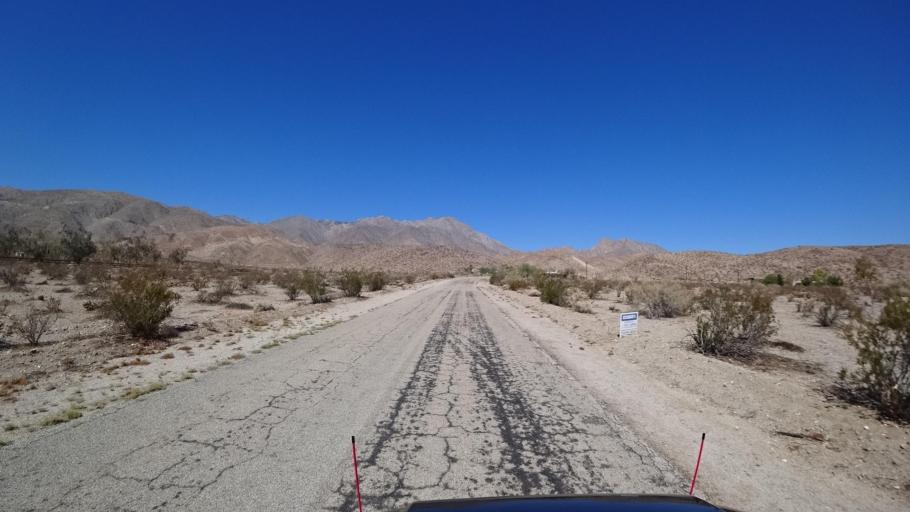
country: US
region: California
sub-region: San Diego County
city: Borrego Springs
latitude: 33.2385
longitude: -116.3856
